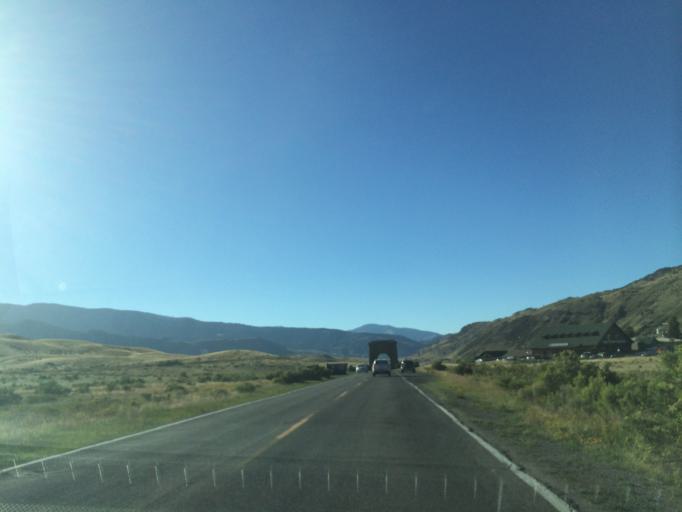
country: US
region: Montana
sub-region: Gallatin County
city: West Yellowstone
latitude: 45.0281
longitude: -110.7058
